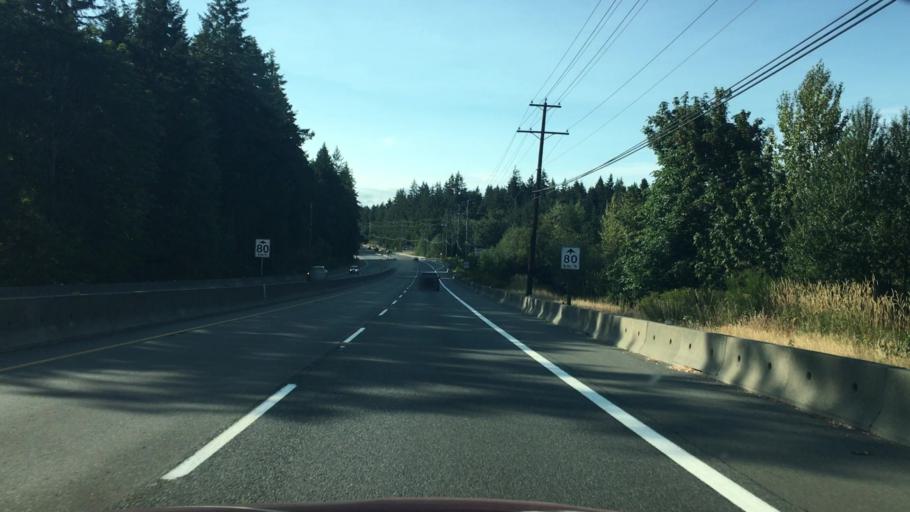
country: CA
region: British Columbia
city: North Cowichan
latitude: 48.9007
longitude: -123.7190
